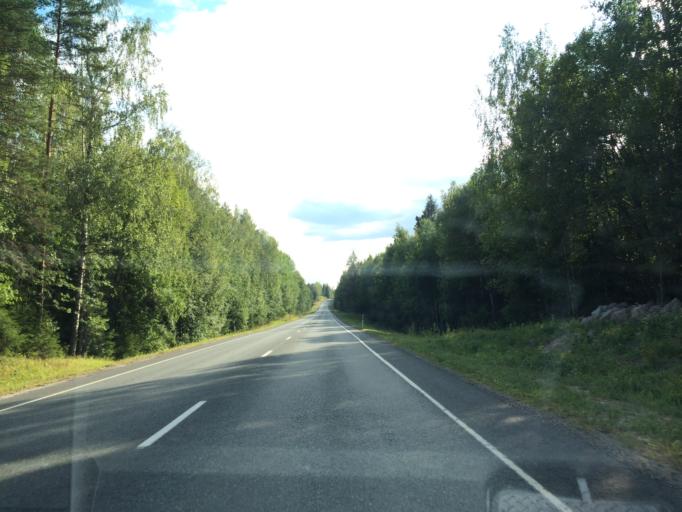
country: FI
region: Haeme
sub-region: Haemeenlinna
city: Haemeenlinna
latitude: 60.9457
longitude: 24.3947
